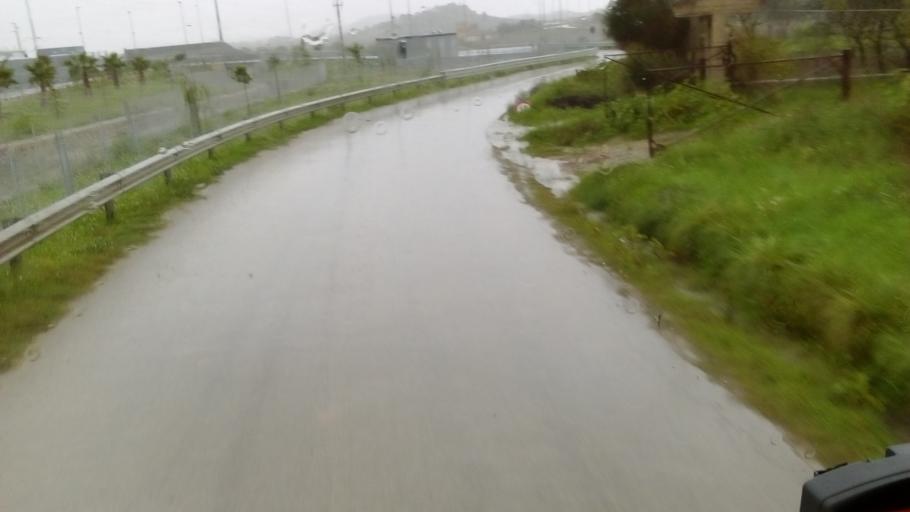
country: IT
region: Sicily
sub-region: Enna
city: Pietraperzia
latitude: 37.4047
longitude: 14.1420
